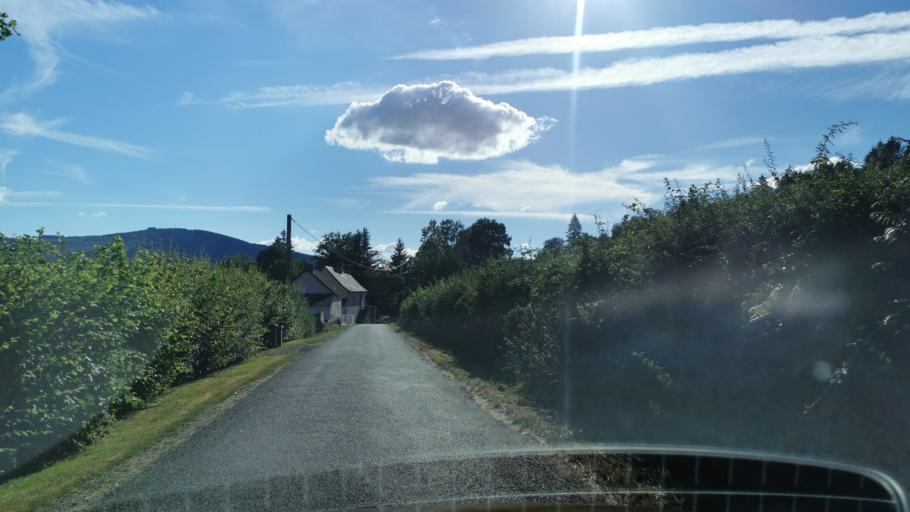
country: FR
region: Bourgogne
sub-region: Departement de Saone-et-Loire
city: Marmagne
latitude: 46.8695
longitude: 4.3236
